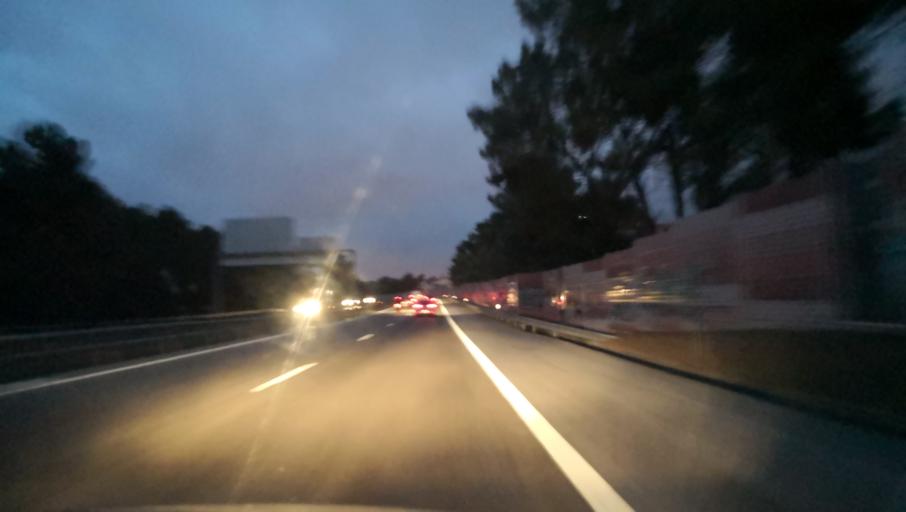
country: PT
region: Setubal
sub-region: Barreiro
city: Santo Antonio da Charneca
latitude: 38.6145
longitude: -9.0277
